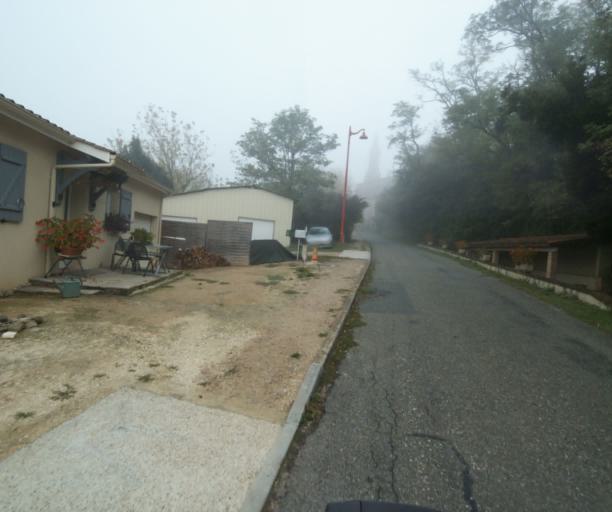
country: FR
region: Midi-Pyrenees
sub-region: Departement du Tarn-et-Garonne
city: Nohic
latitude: 43.9232
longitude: 1.4694
